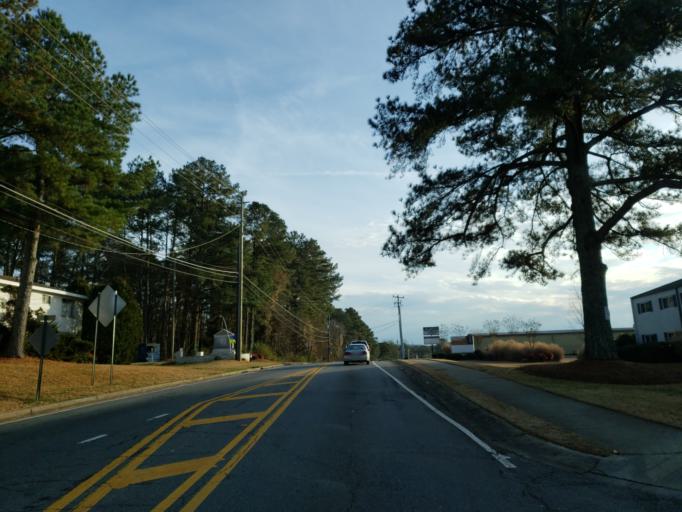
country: US
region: Georgia
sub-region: Cobb County
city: Fair Oaks
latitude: 33.9280
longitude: -84.5549
